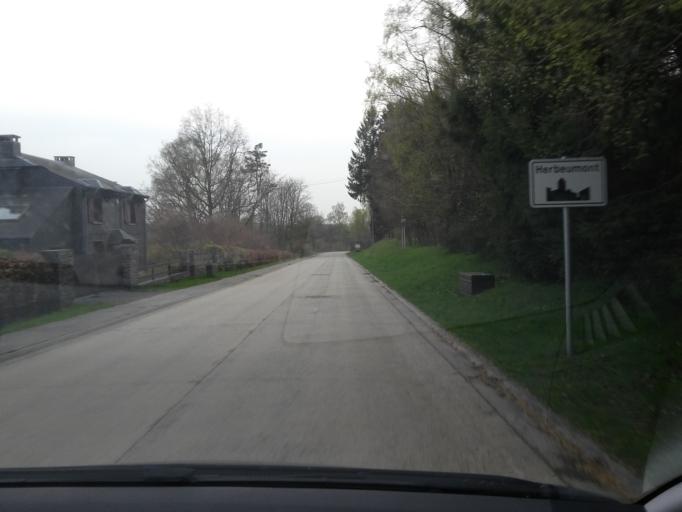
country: BE
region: Wallonia
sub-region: Province du Luxembourg
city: Herbeumont
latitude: 49.7873
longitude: 5.2519
